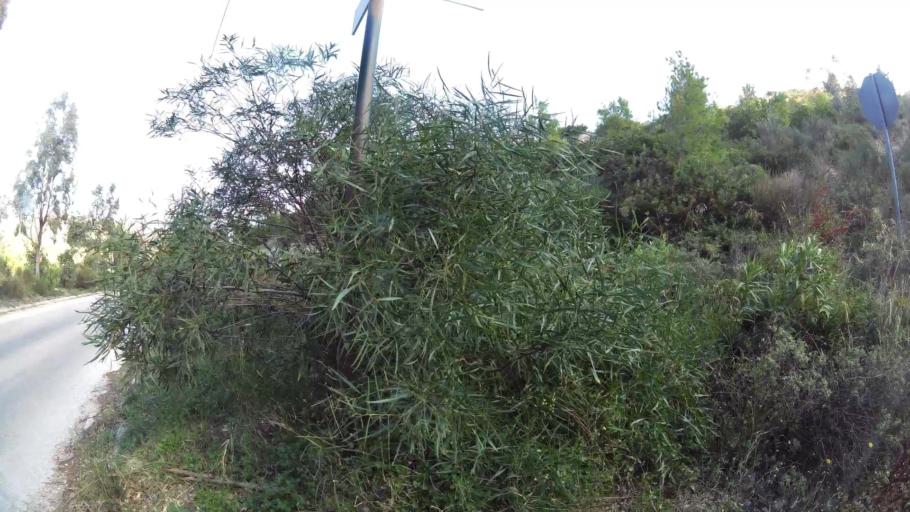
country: GR
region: Attica
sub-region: Nomarchia Anatolikis Attikis
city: Dhrafi
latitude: 38.0202
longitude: 23.9151
